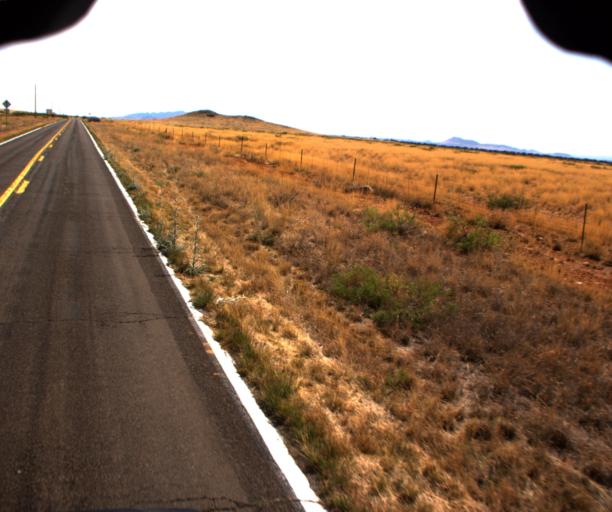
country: US
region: Arizona
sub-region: Cochise County
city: Willcox
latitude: 31.9668
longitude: -109.4770
